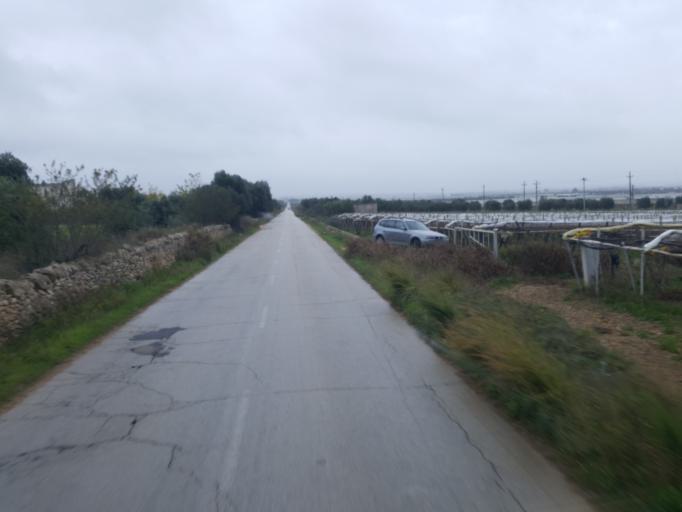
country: IT
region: Apulia
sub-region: Provincia di Taranto
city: Montemesola
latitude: 40.5481
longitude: 17.3579
